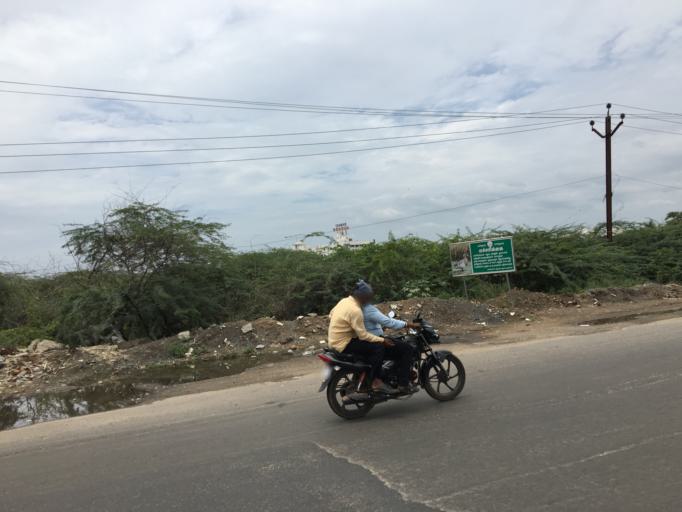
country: IN
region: Tamil Nadu
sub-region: Kancheepuram
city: Madipakkam
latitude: 12.9454
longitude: 80.2088
